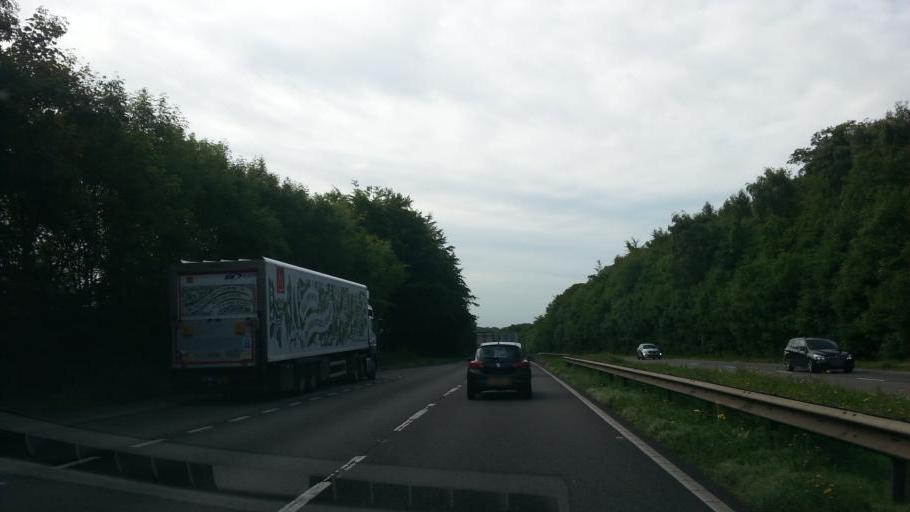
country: GB
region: England
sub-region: Lincolnshire
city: Grantham
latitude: 52.8453
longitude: -0.6282
